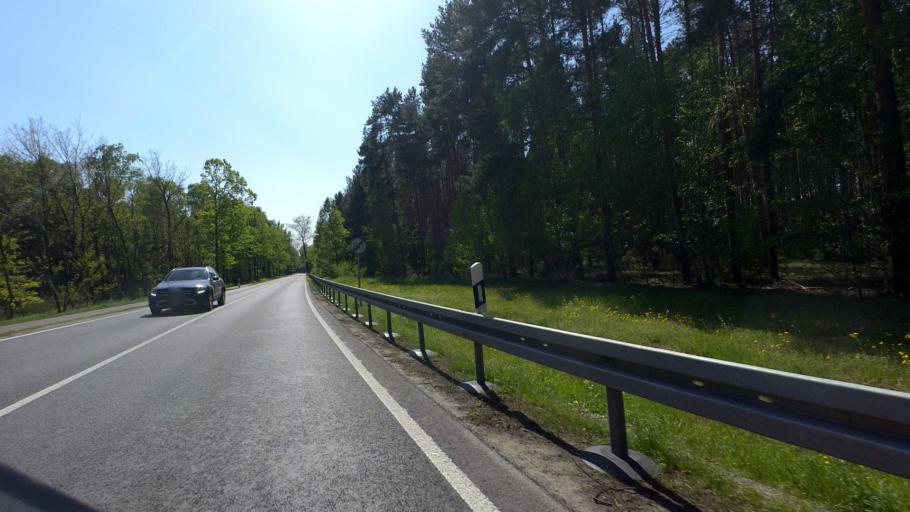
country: DE
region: Brandenburg
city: Beeskow
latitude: 52.1485
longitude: 14.2133
